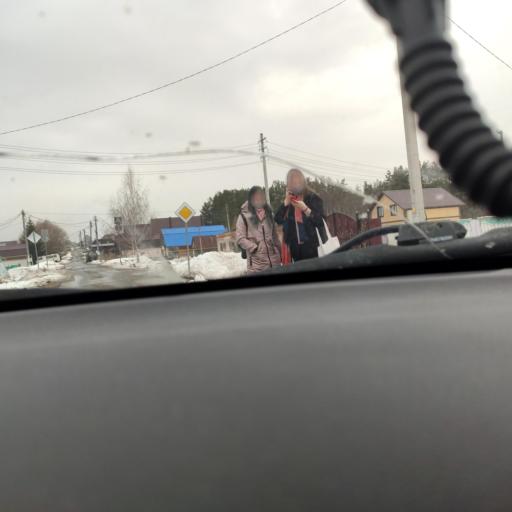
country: RU
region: Tatarstan
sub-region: Gorod Kazan'
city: Kazan
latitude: 55.8990
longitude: 49.1391
